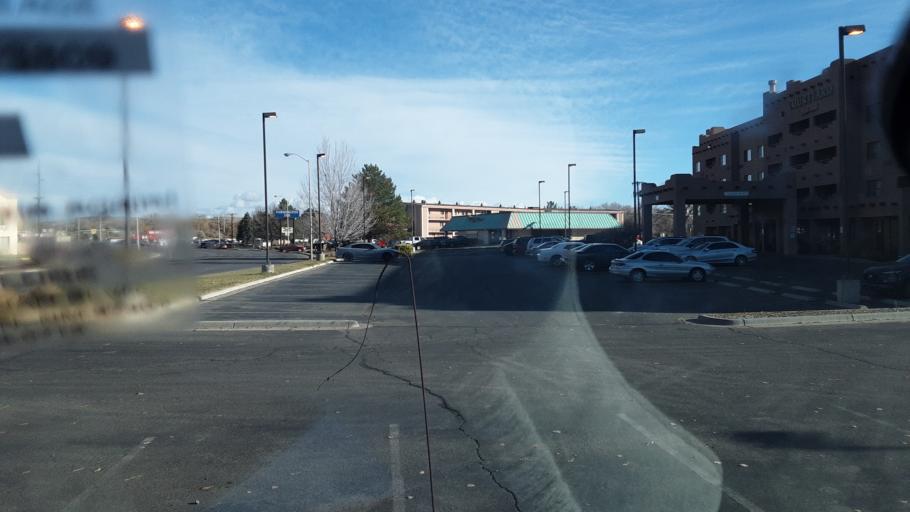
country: US
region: New Mexico
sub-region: San Juan County
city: Farmington
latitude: 36.7301
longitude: -108.1897
